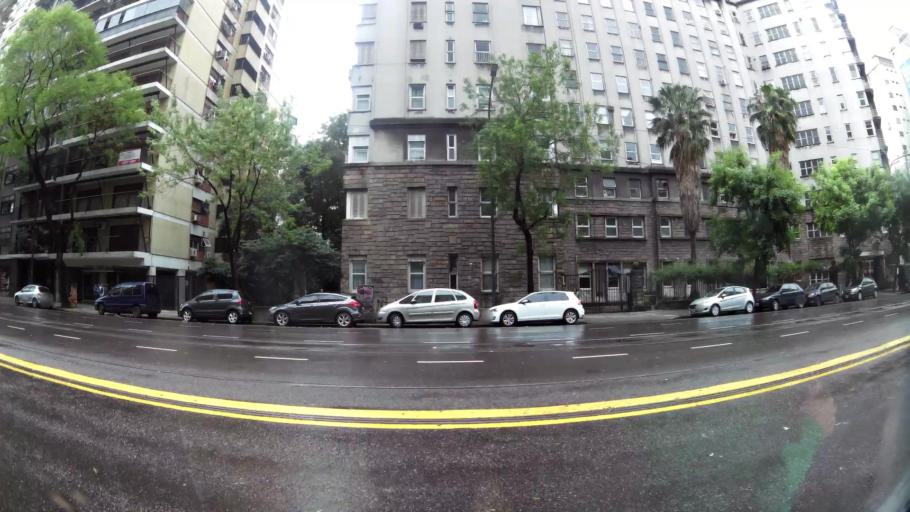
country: AR
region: Buenos Aires F.D.
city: Retiro
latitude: -34.5819
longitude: -58.4133
